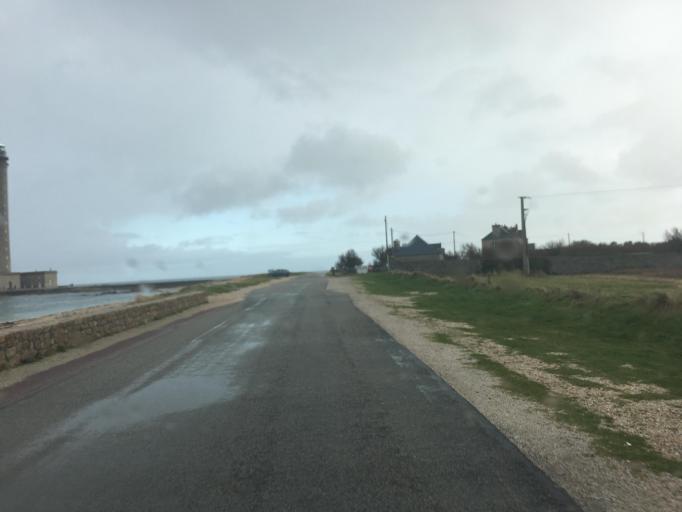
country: FR
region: Lower Normandy
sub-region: Departement de la Manche
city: Reville
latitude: 49.6951
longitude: -1.2700
